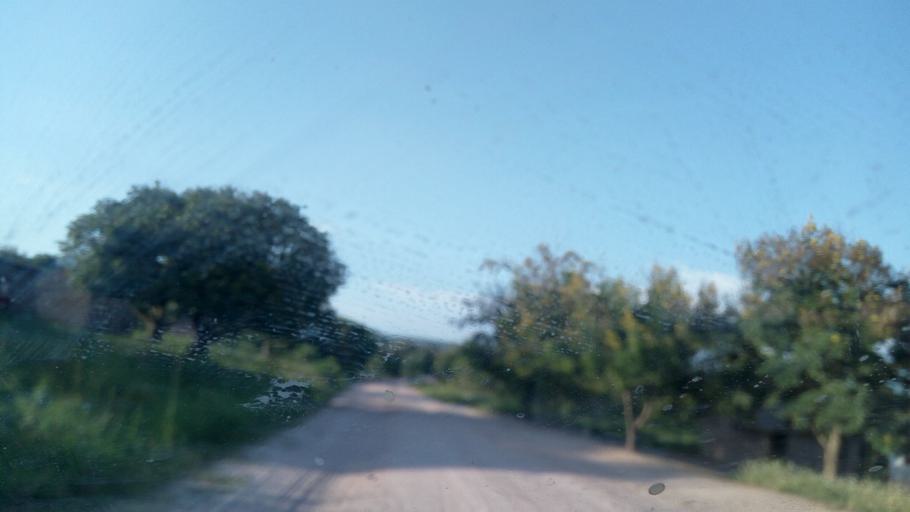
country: BI
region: Bururi
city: Rumonge
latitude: -4.1793
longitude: 29.0582
